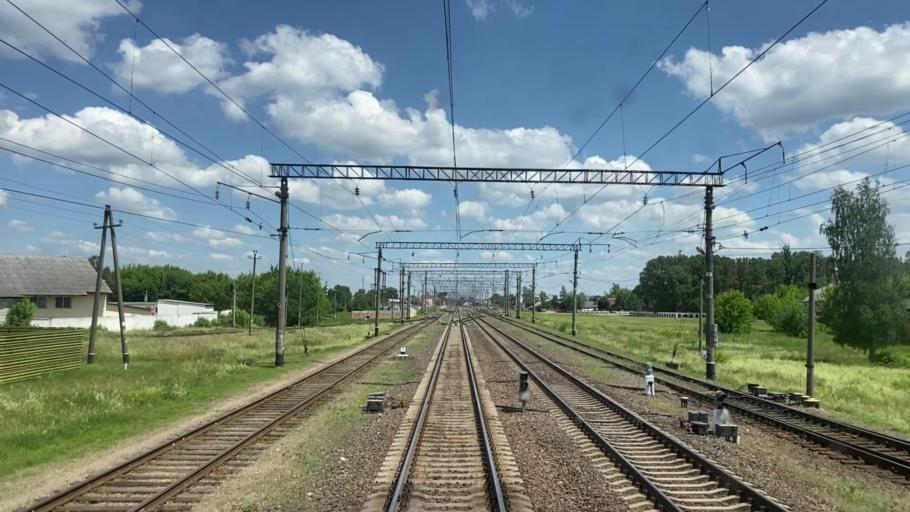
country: BY
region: Brest
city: Ivatsevichy
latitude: 52.7029
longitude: 25.3308
